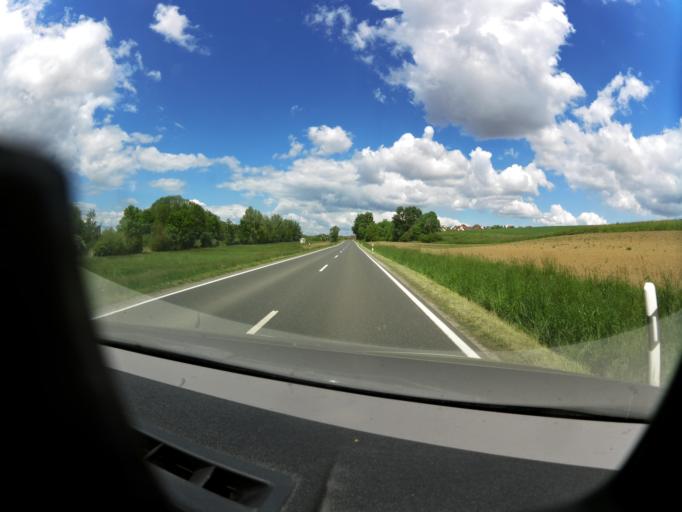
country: DE
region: Bavaria
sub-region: Regierungsbezirk Unterfranken
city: Prosselsheim
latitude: 49.8708
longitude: 10.1274
